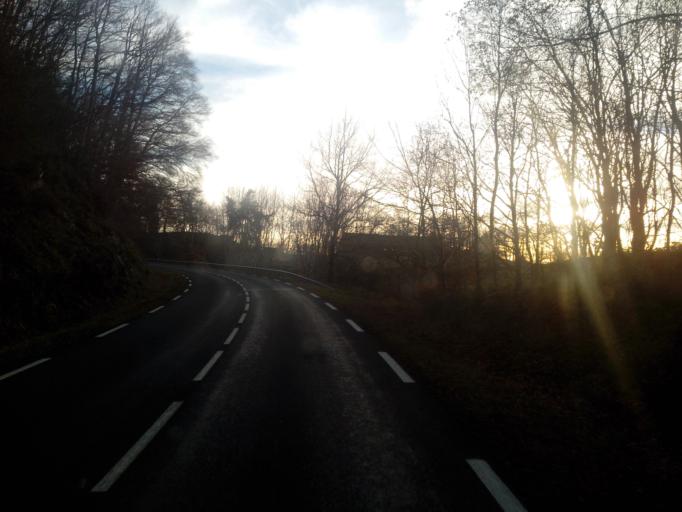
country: FR
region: Auvergne
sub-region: Departement du Cantal
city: Riom-es-Montagnes
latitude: 45.3075
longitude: 2.6055
